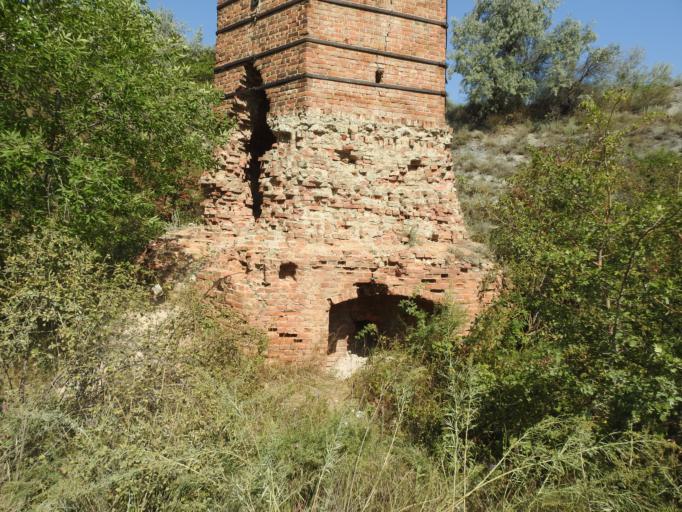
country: RU
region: Saratov
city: Kamenskiy
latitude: 50.6151
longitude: 45.6530
